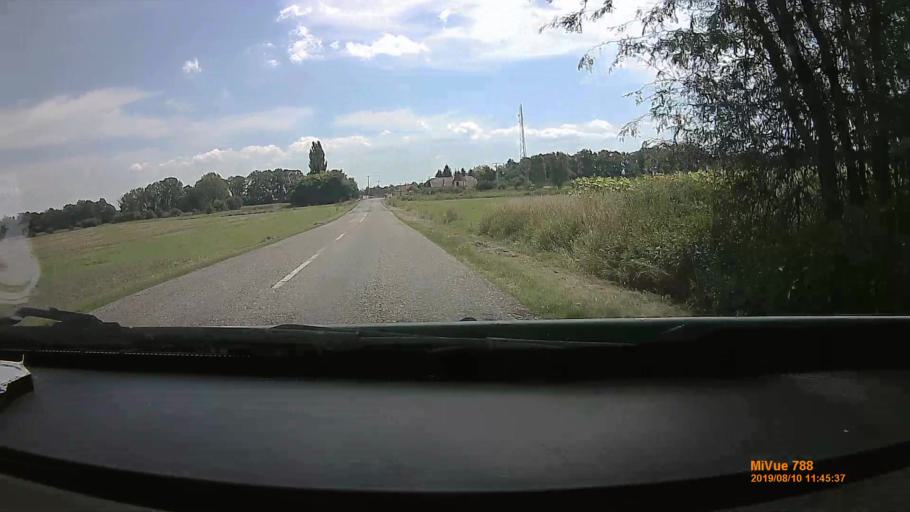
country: HU
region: Borsod-Abauj-Zemplen
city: Szentistvan
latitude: 47.7165
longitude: 20.6308
